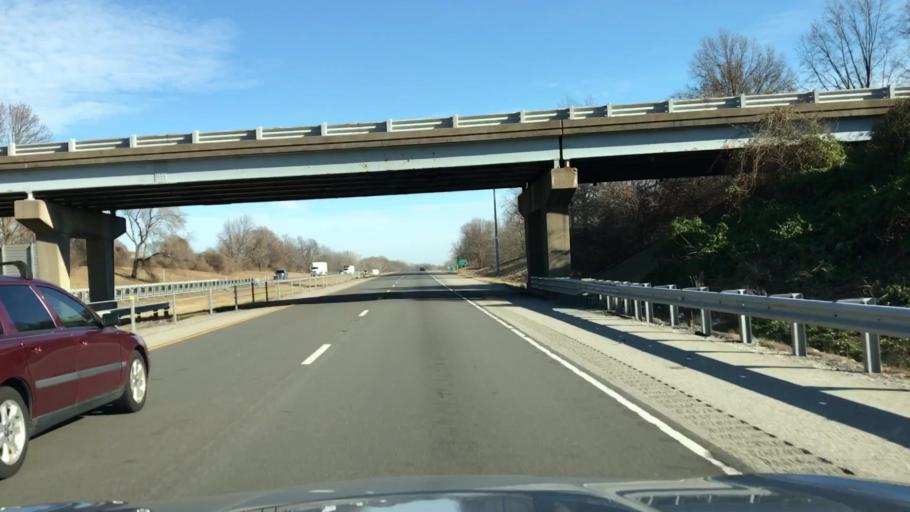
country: US
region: Illinois
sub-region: Madison County
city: Glen Carbon
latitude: 38.7568
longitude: -89.9751
